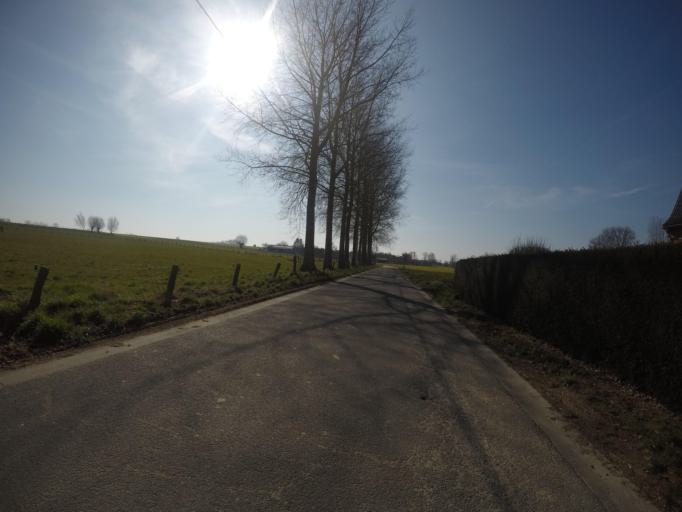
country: BE
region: Flanders
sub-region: Provincie Oost-Vlaanderen
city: Sint-Maria-Lierde
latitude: 50.7957
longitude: 3.8410
